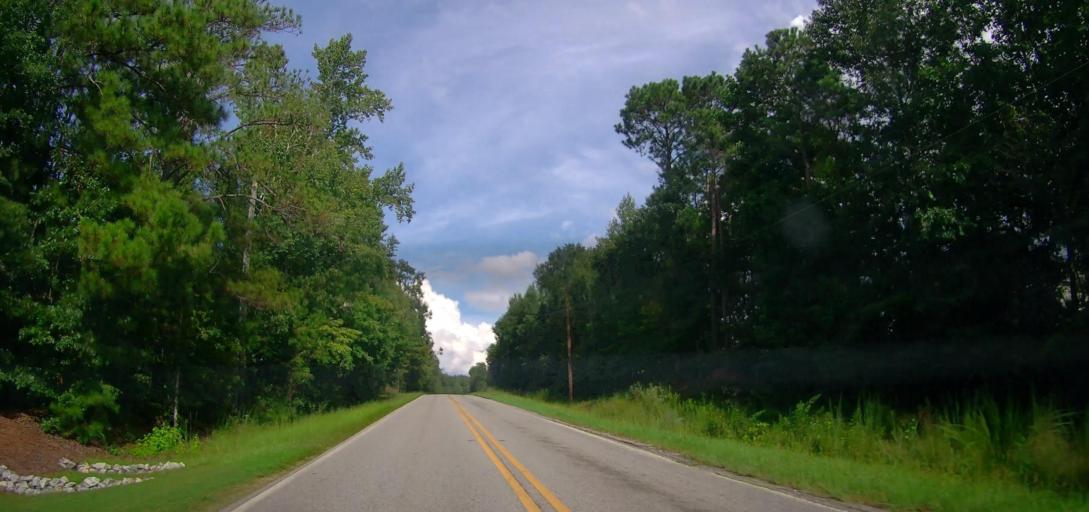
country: US
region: Alabama
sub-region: Russell County
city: Phenix City
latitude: 32.5896
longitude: -84.9176
